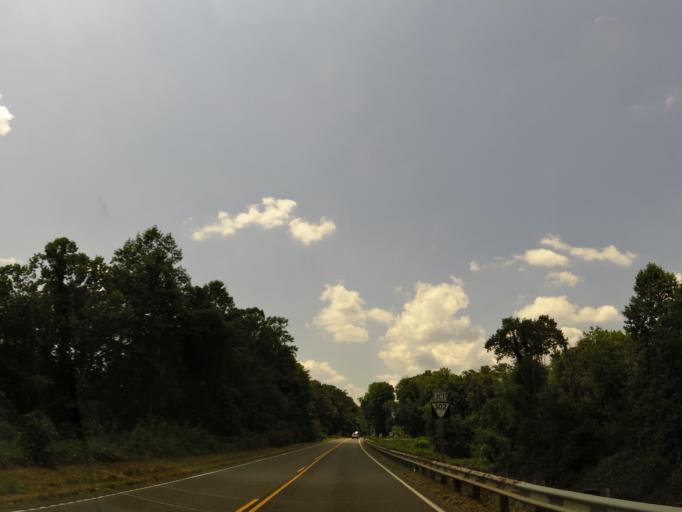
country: US
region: Tennessee
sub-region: Rhea County
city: Spring City
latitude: 35.6472
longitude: -84.8615
